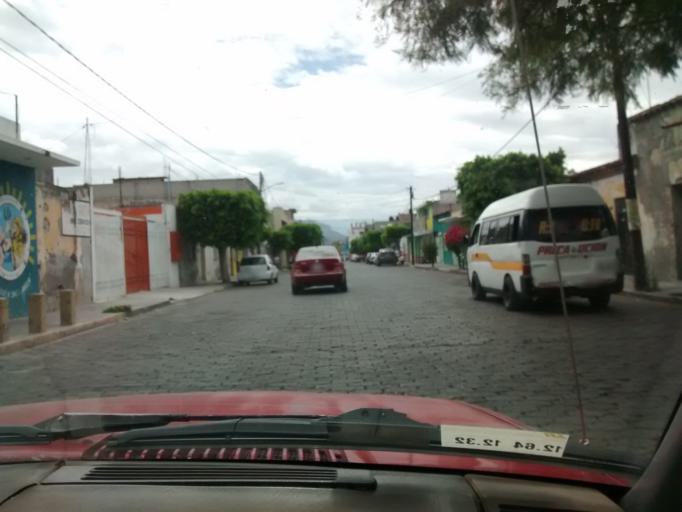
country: MX
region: Puebla
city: Tehuacan
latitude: 18.4673
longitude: -97.4000
